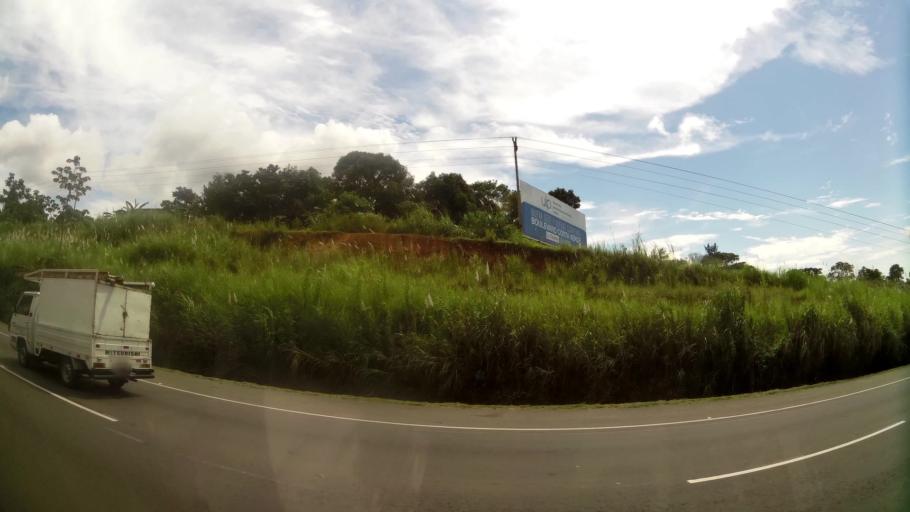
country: PA
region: Panama
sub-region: Distrito Arraijan
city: Arraijan
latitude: 8.9441
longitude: -79.6719
